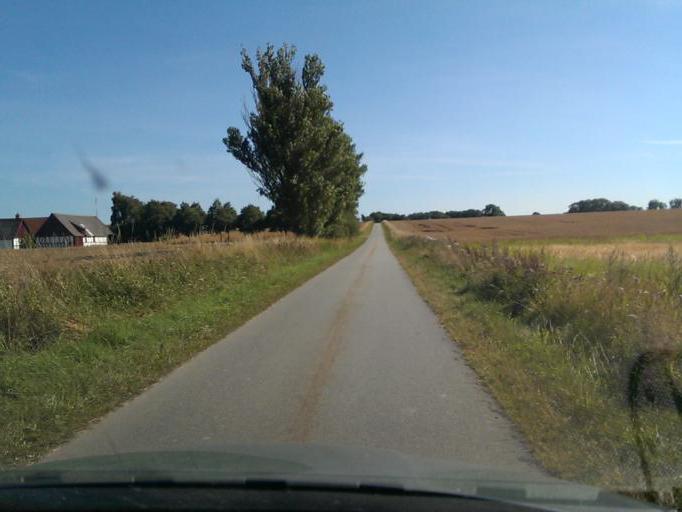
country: DK
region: Central Jutland
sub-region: Odder Kommune
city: Odder
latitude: 55.8633
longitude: 10.0623
